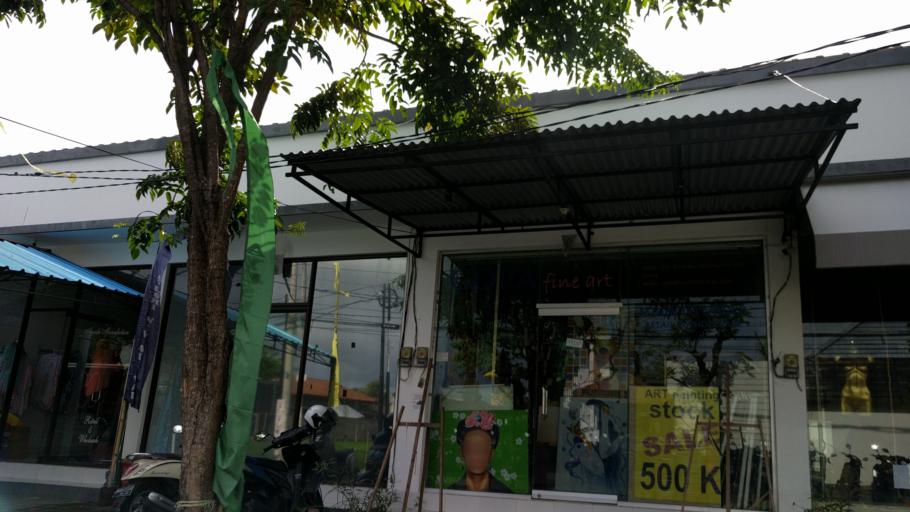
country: ID
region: Bali
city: Kuta
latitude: -8.6810
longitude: 115.1629
